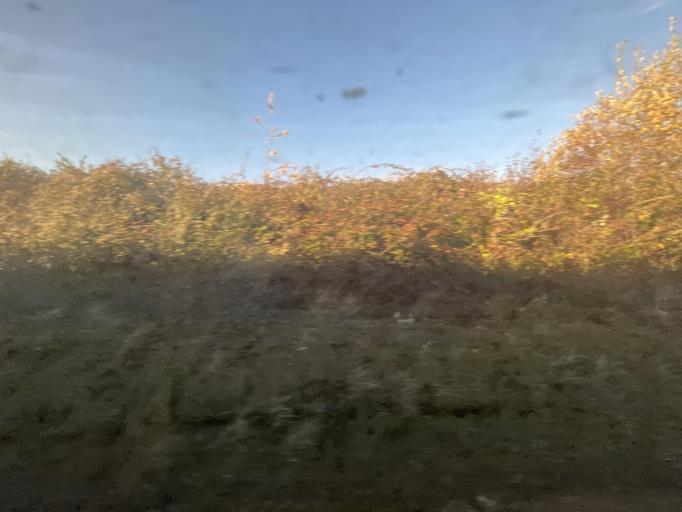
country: FR
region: Pays de la Loire
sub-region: Departement de la Loire-Atlantique
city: Sainte-Luce-sur-Loire
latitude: 47.2507
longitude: -1.4650
